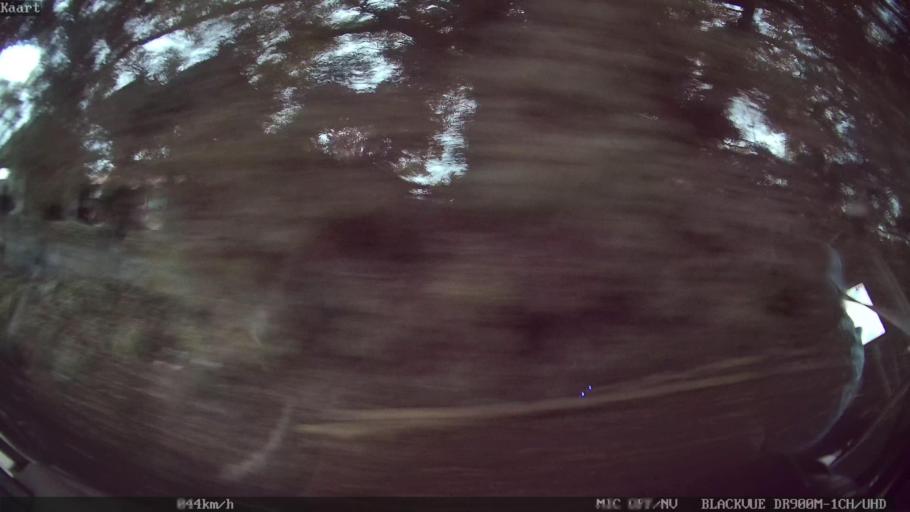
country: ID
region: Bali
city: Banjar Bias
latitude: -8.3203
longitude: 115.4049
